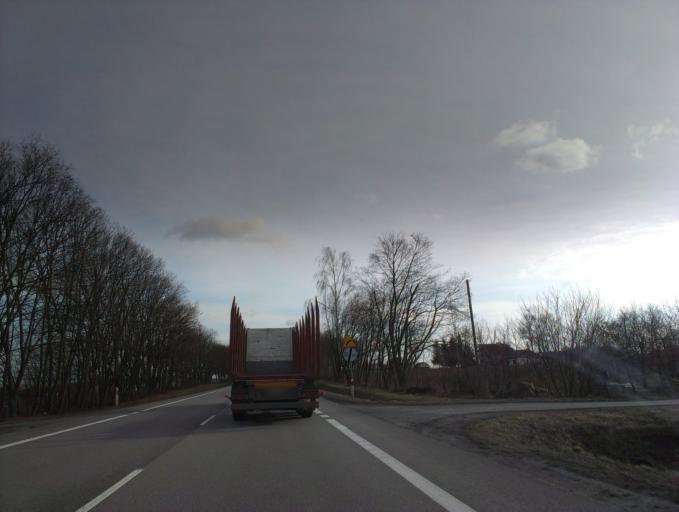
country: PL
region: Kujawsko-Pomorskie
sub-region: Powiat lipnowski
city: Kikol
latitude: 52.8811
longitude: 19.1399
